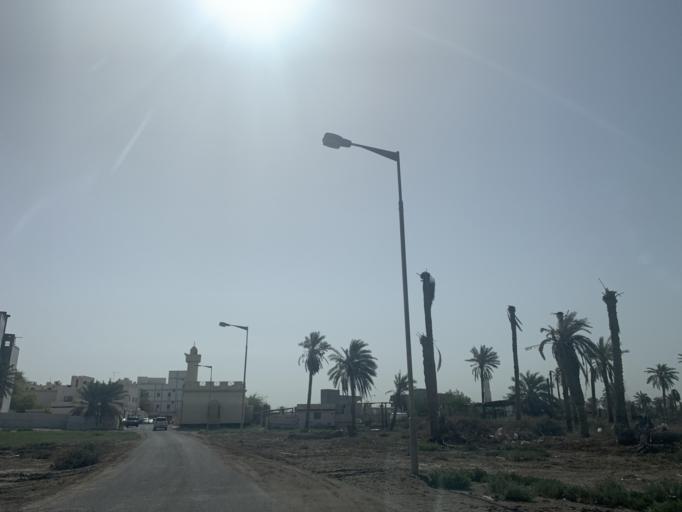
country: BH
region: Manama
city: Jidd Hafs
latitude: 26.2023
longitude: 50.5504
